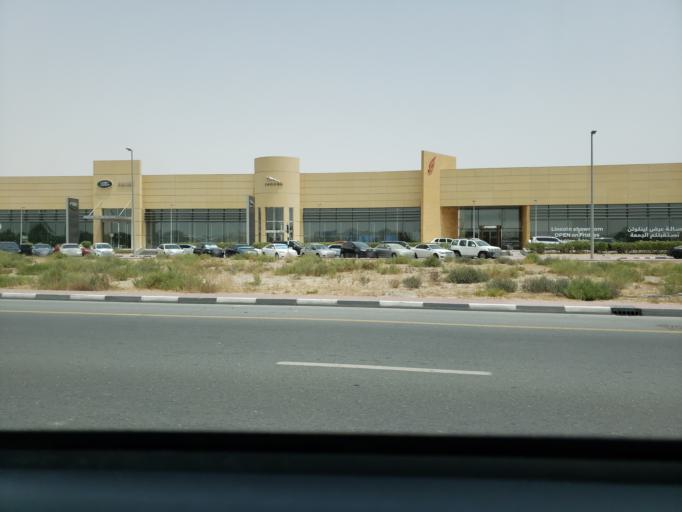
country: AE
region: Ash Shariqah
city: Sharjah
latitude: 25.3477
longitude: 55.4751
